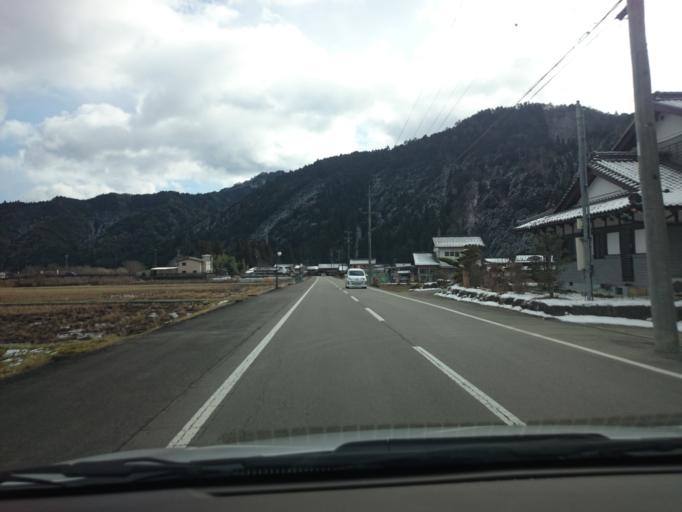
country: JP
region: Gifu
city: Gujo
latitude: 35.7414
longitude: 137.0687
